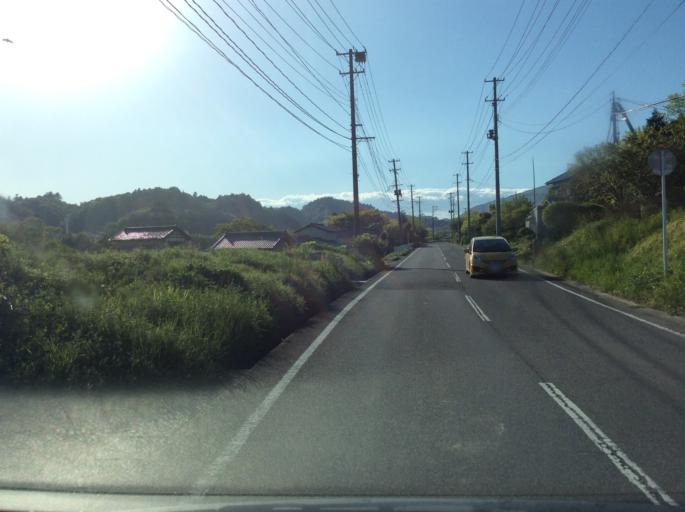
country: JP
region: Fukushima
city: Iwaki
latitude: 36.9862
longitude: 140.8338
